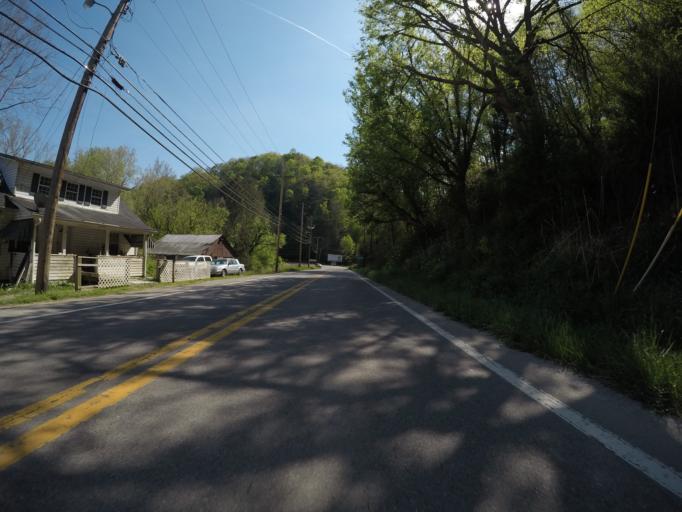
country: US
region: West Virginia
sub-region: Kanawha County
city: Clendenin
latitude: 38.4951
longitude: -81.3529
